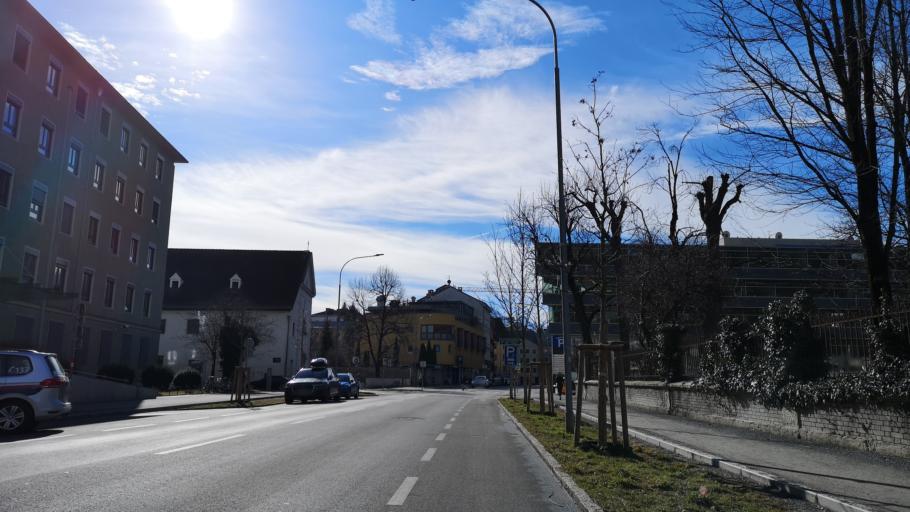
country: AT
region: Tyrol
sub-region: Innsbruck Stadt
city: Innsbruck
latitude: 47.2708
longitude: 11.4000
